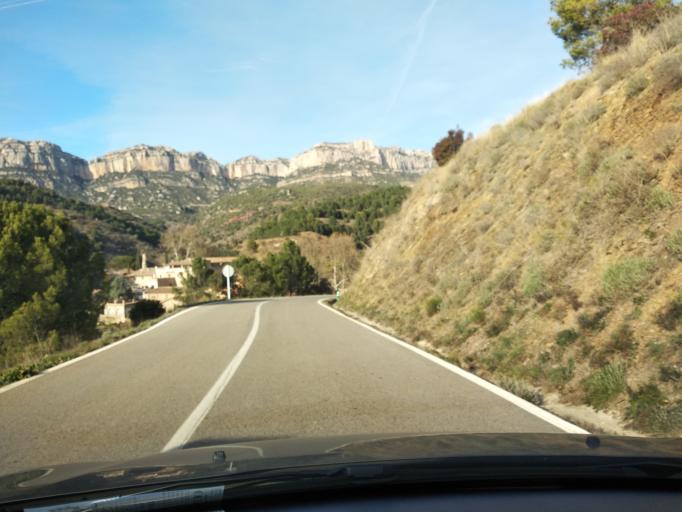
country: ES
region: Catalonia
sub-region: Provincia de Tarragona
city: la Morera de Montsant
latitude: 41.2460
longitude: 0.8109
